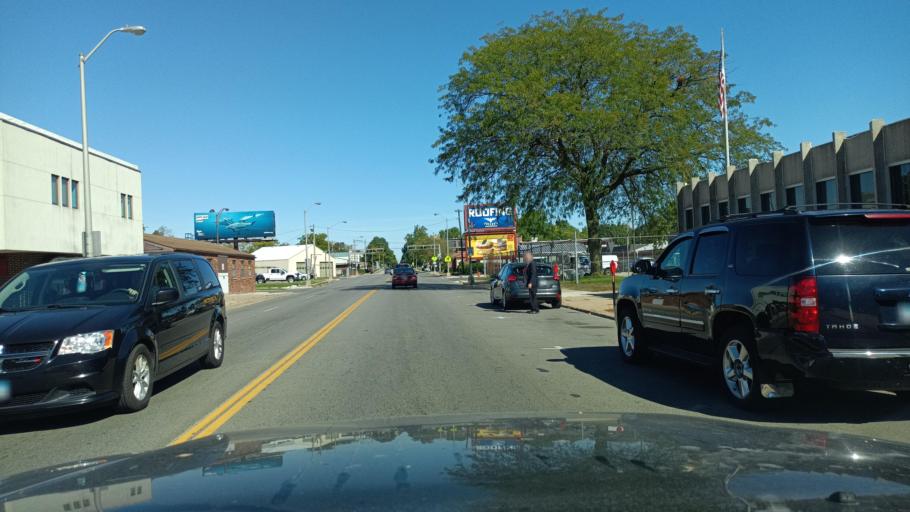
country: US
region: Illinois
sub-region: Champaign County
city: Champaign
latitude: 40.1214
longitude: -88.2435
